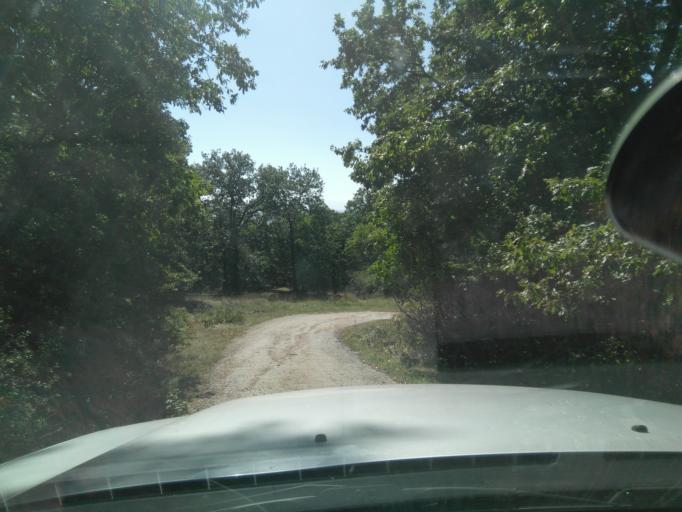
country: HU
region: Fejer
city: Velence
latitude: 47.2585
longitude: 18.5964
